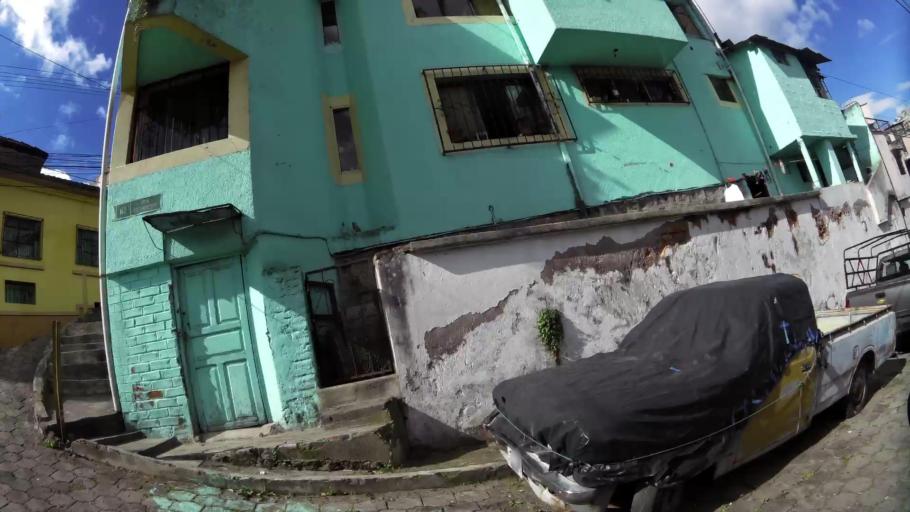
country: EC
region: Pichincha
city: Quito
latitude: -0.2294
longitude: -78.5053
